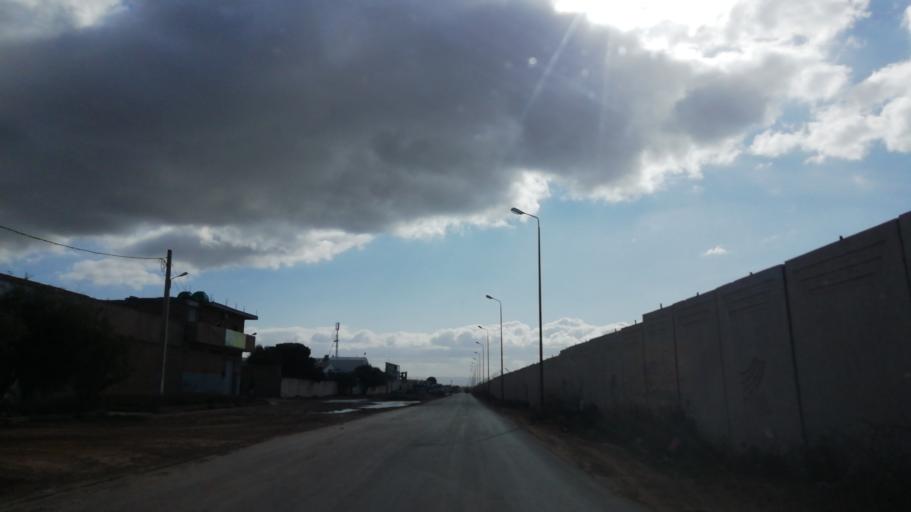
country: DZ
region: Oran
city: Es Senia
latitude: 35.6389
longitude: -0.5996
